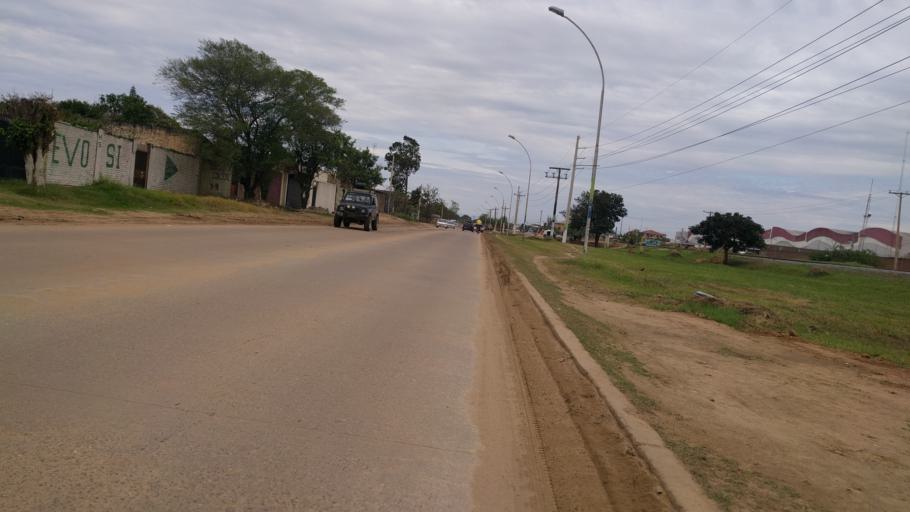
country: BO
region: Santa Cruz
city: Santa Cruz de la Sierra
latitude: -17.8498
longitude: -63.1790
